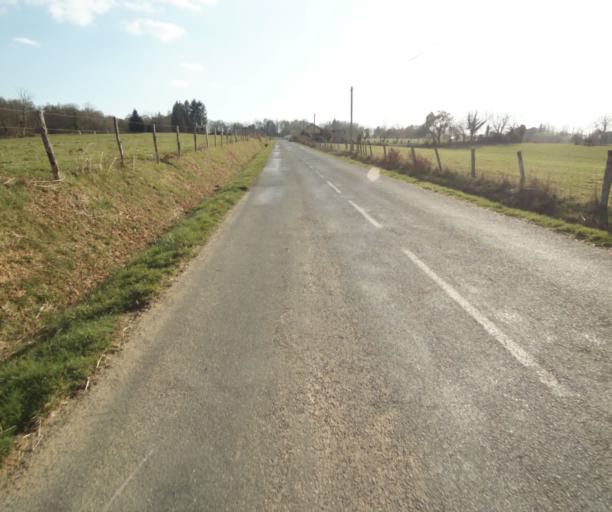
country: FR
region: Limousin
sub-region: Departement de la Correze
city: Saint-Mexant
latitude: 45.3391
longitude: 1.6178
